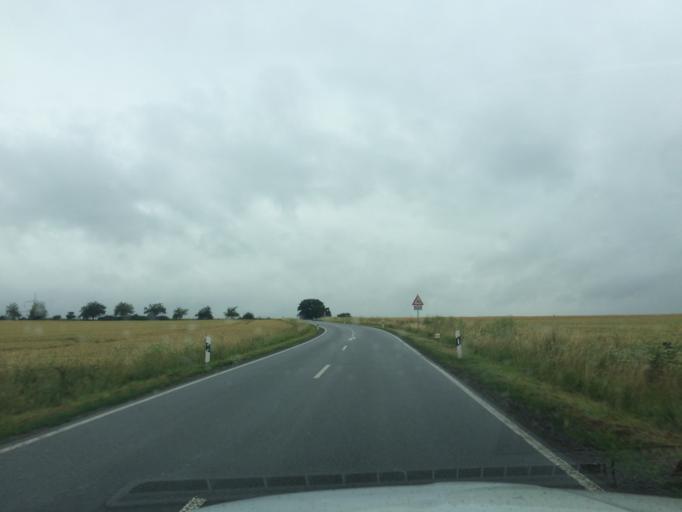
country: DE
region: Hesse
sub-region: Regierungsbezirk Kassel
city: Hofgeismar
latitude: 51.5229
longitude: 9.4180
